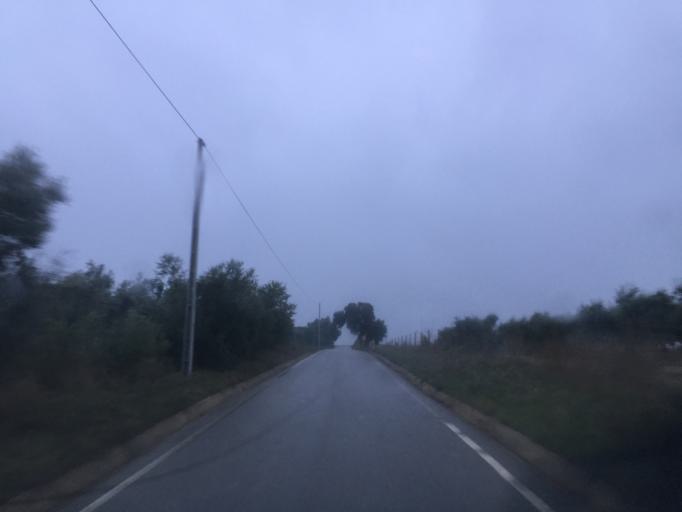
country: PT
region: Portalegre
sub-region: Avis
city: Avis
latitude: 39.0421
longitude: -7.9109
